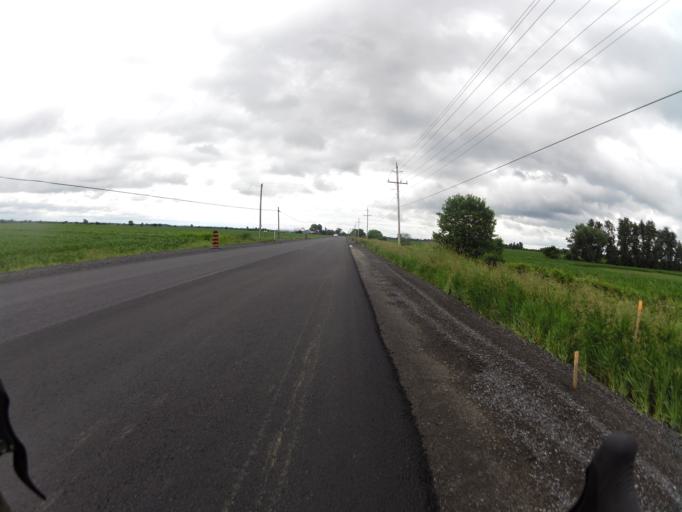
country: CA
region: Ontario
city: Bells Corners
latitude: 45.2263
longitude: -75.8603
